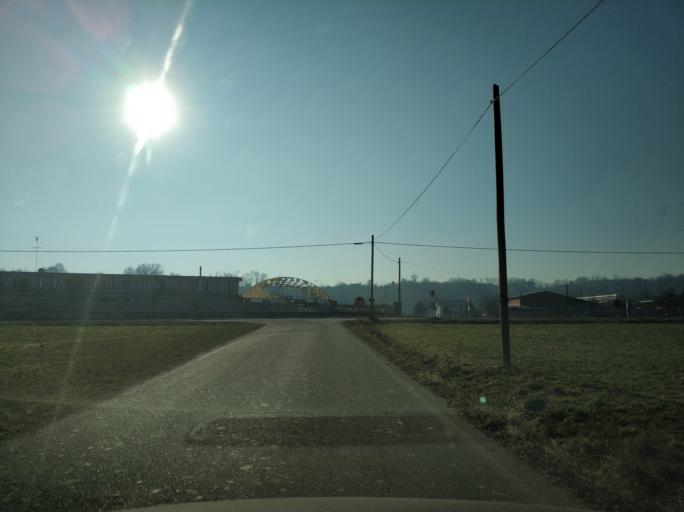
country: IT
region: Piedmont
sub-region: Provincia di Torino
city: Levone
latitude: 45.2990
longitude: 7.6146
